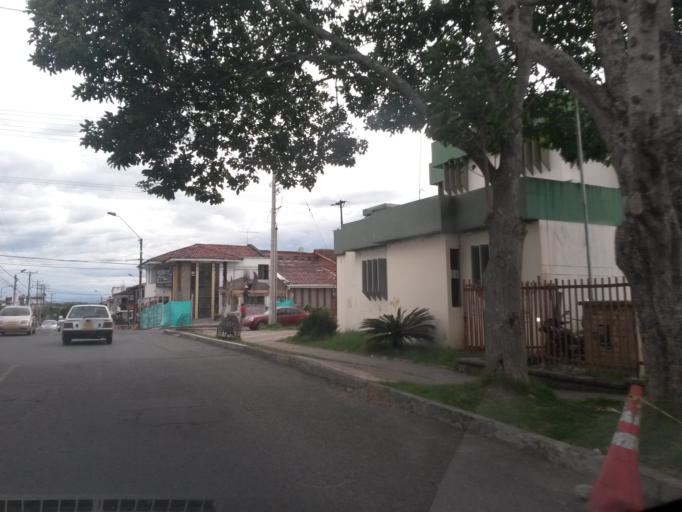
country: CO
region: Cauca
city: Popayan
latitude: 2.4547
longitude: -76.6025
